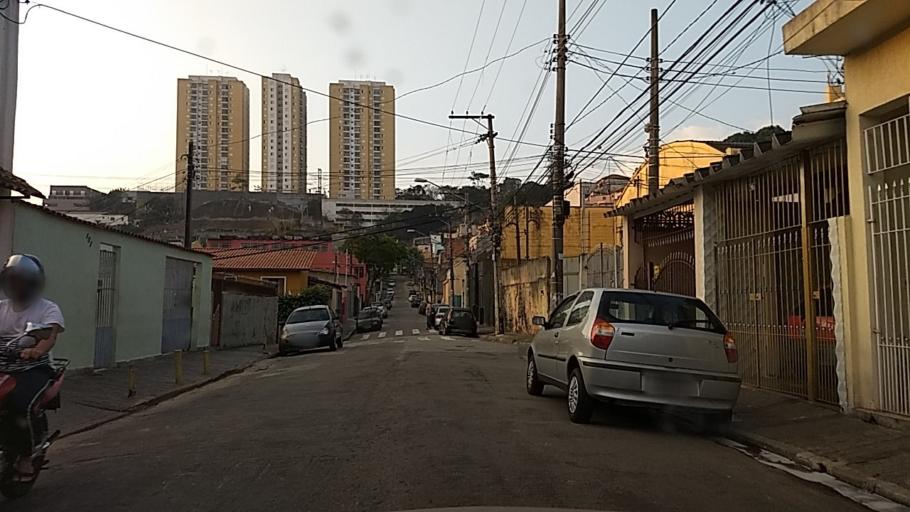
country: BR
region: Sao Paulo
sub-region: Sao Paulo
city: Sao Paulo
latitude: -23.5024
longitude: -46.5946
